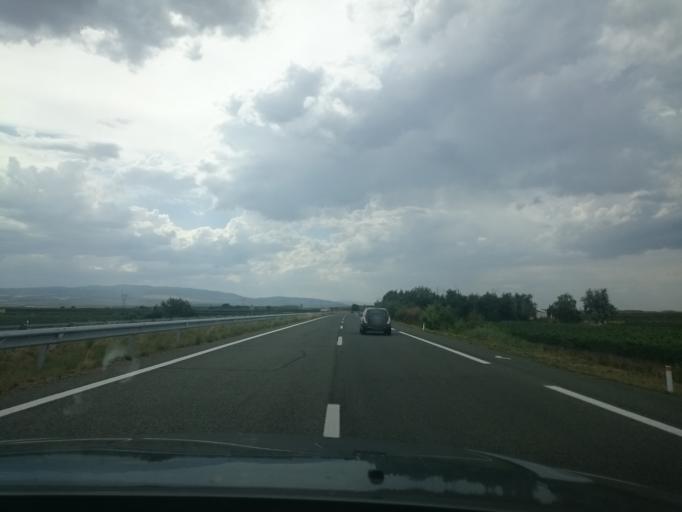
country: ES
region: Navarre
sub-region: Provincia de Navarra
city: Corella
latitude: 42.1513
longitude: -1.7990
